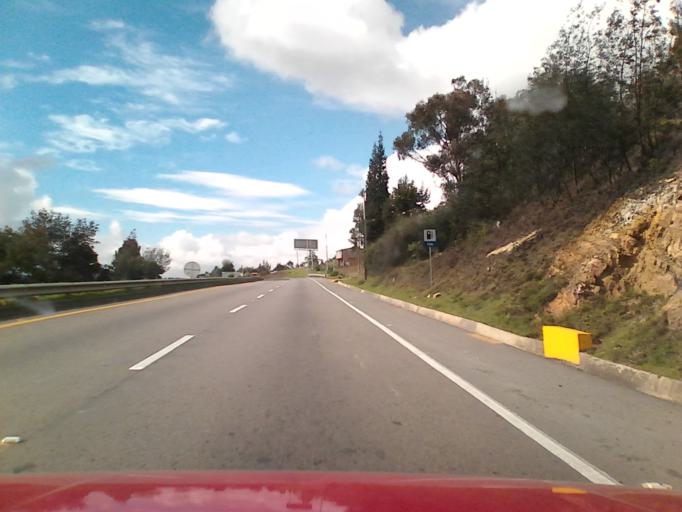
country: CO
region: Boyaca
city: Combita
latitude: 5.6109
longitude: -73.3248
